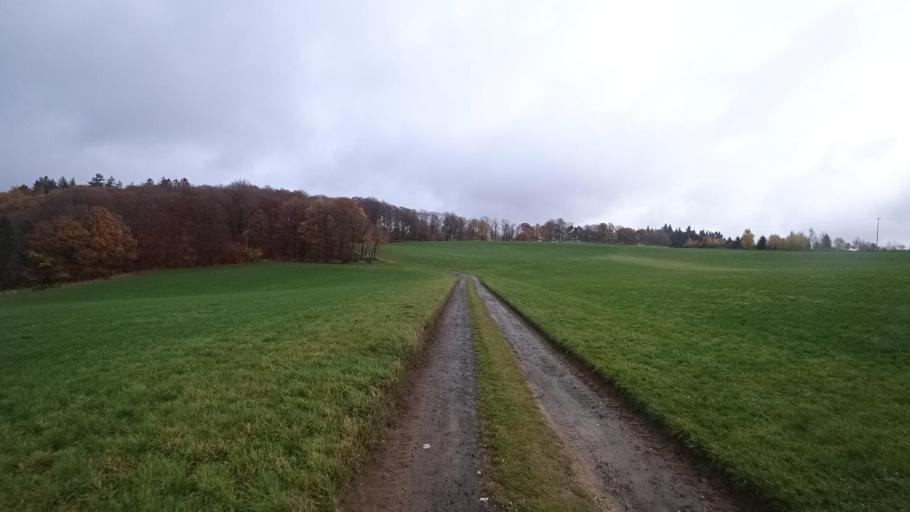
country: DE
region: Rheinland-Pfalz
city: Spessart
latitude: 50.4904
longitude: 7.1069
